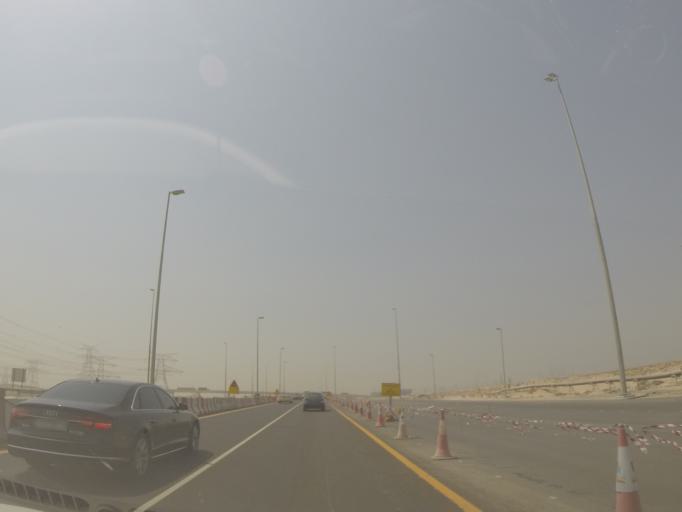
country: AE
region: Dubai
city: Dubai
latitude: 25.0125
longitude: 55.1654
